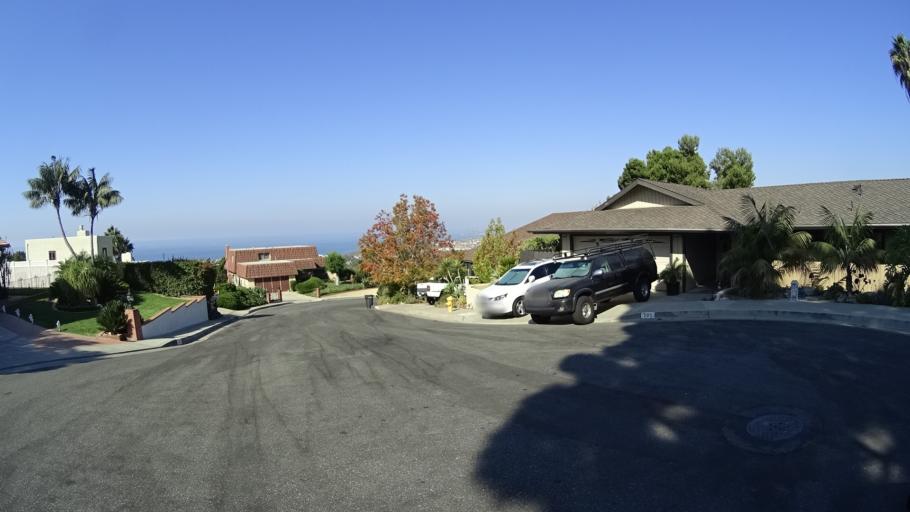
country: US
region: California
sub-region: Orange County
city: San Clemente
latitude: 33.4330
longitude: -117.6102
